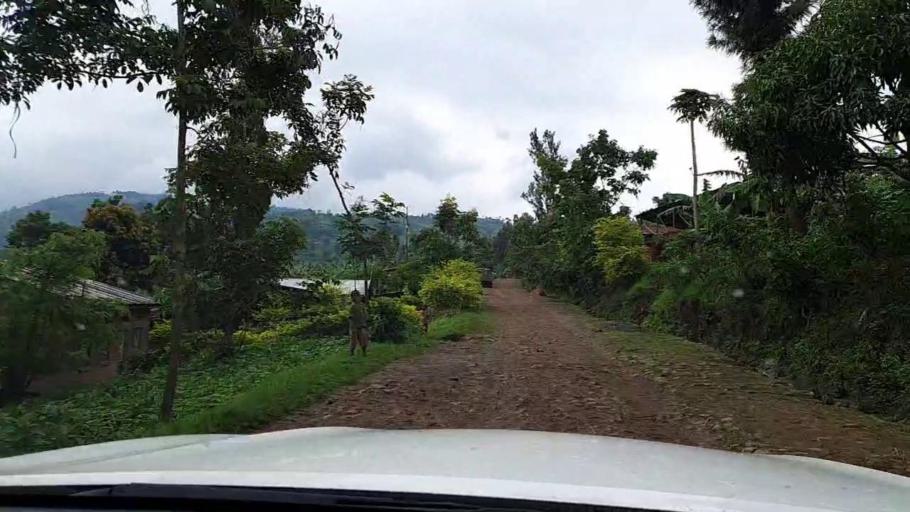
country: RW
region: Western Province
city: Cyangugu
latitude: -2.5475
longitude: 29.0380
